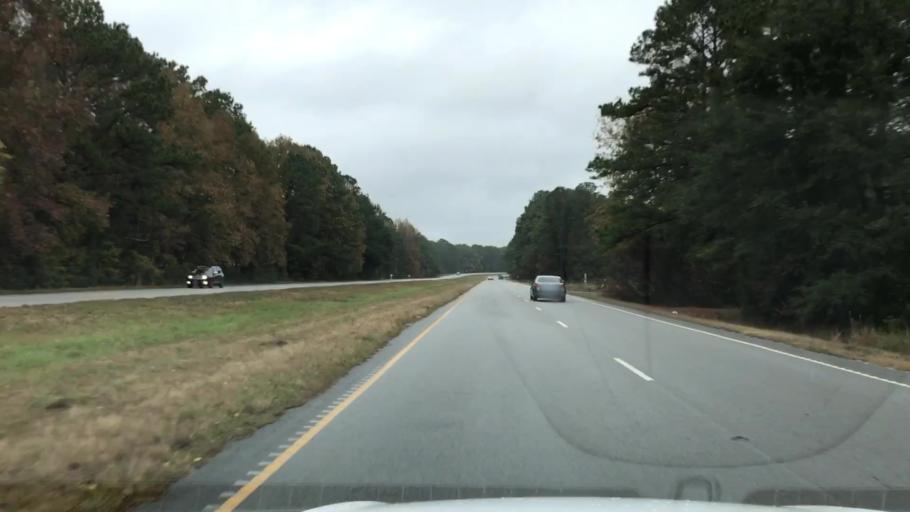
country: US
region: South Carolina
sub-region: Charleston County
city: Awendaw
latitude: 32.9309
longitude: -79.7133
